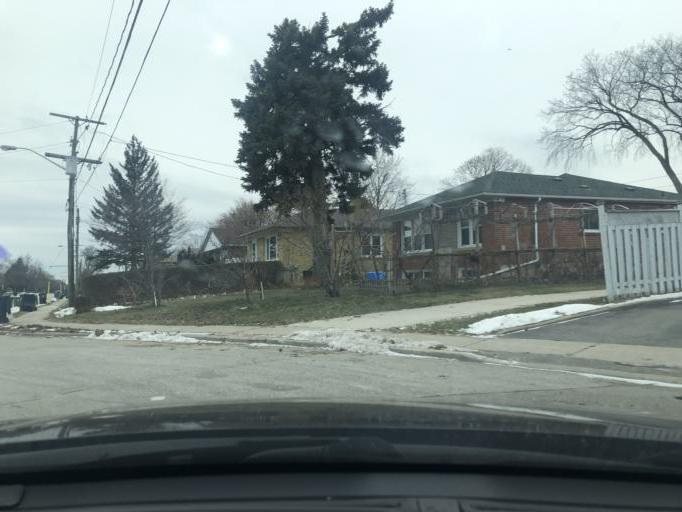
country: CA
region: Ontario
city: Scarborough
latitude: 43.7686
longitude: -79.3083
